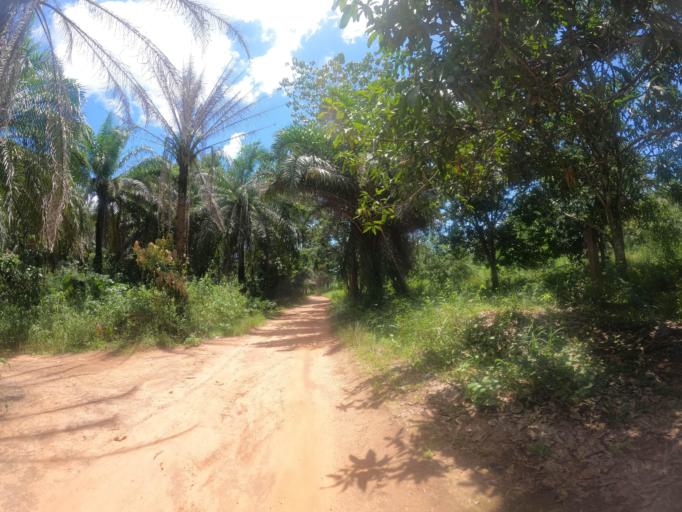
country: SL
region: Northern Province
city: Makeni
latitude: 8.8590
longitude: -12.1109
